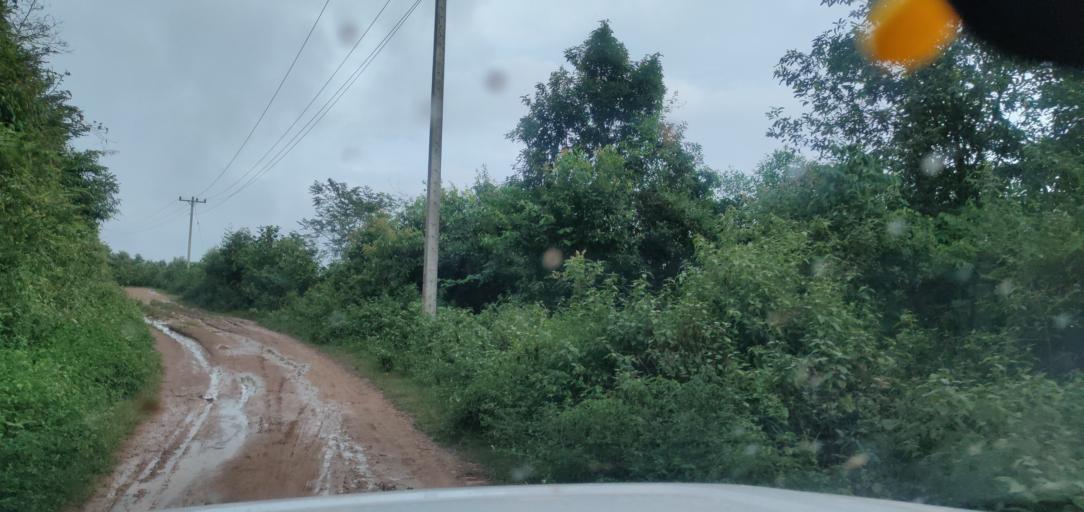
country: LA
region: Phongsali
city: Phongsali
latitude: 21.4477
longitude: 102.2875
